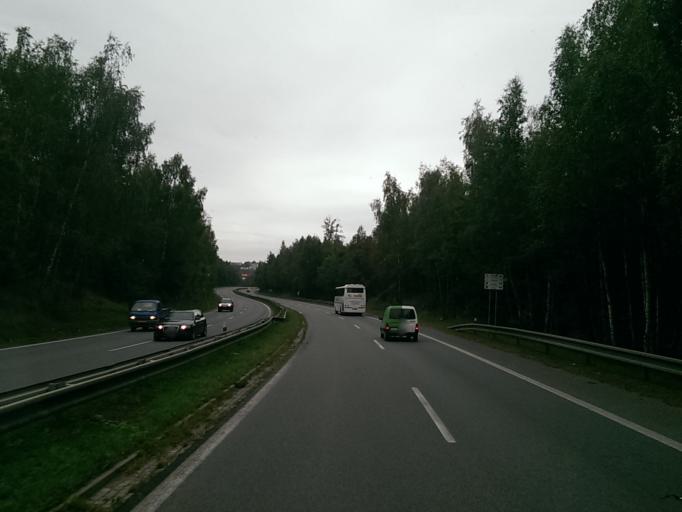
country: CZ
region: Vysocina
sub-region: Okres Jihlava
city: Jihlava
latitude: 49.4174
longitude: 15.5788
